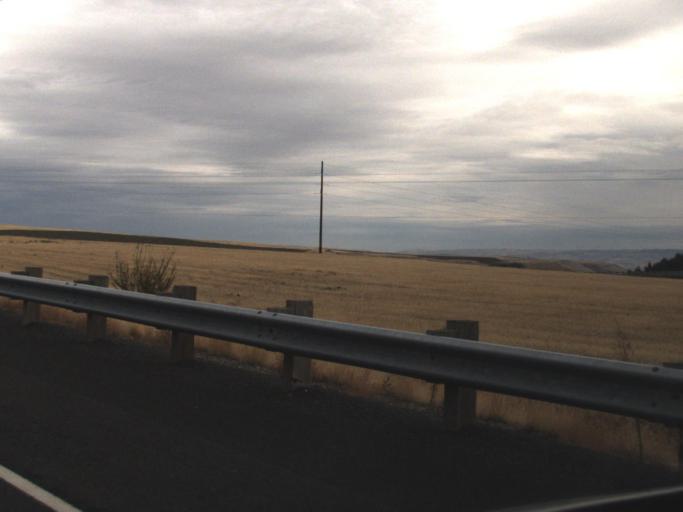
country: US
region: Washington
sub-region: Asotin County
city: Clarkston
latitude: 46.4744
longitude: -117.0465
